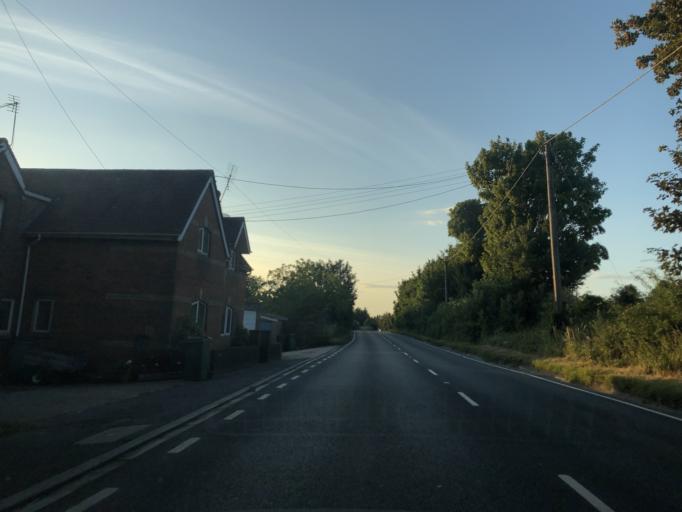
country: GB
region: England
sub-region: Isle of Wight
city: Newport
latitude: 50.6783
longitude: -1.2845
